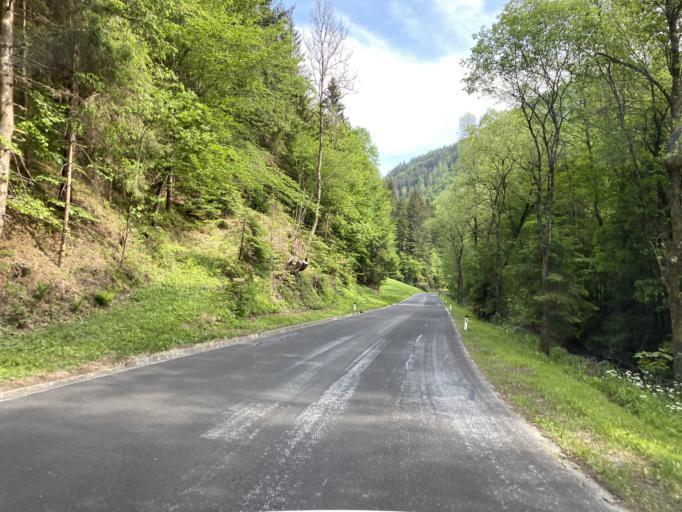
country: AT
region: Styria
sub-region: Politischer Bezirk Weiz
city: Koglhof
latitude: 47.3109
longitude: 15.6570
